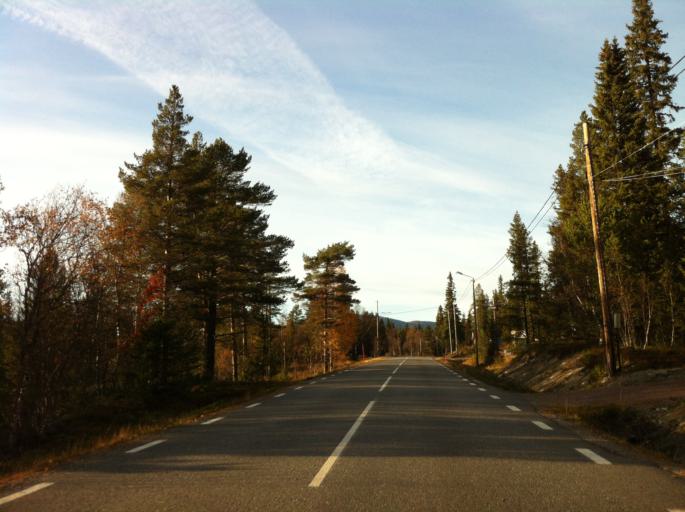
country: NO
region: Hedmark
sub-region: Engerdal
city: Engerdal
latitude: 62.0674
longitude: 12.3165
